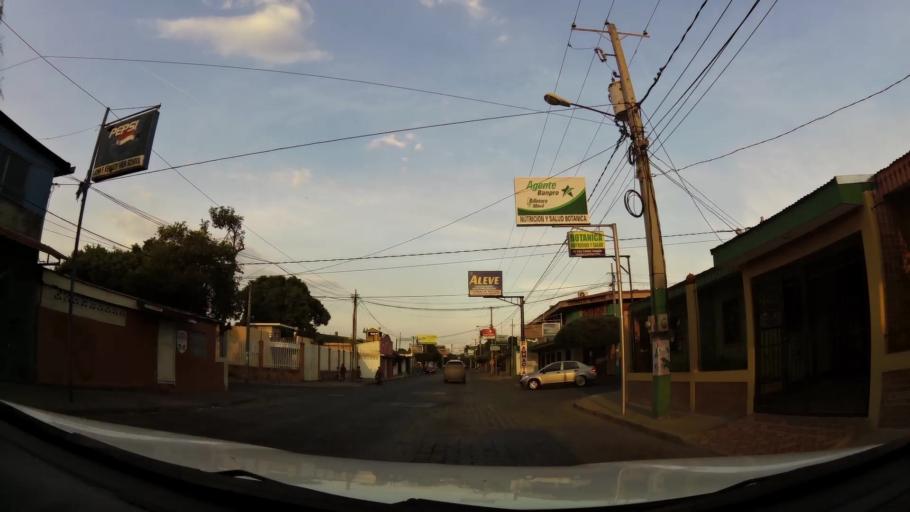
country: NI
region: Managua
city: Managua
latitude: 12.1419
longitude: -86.2478
